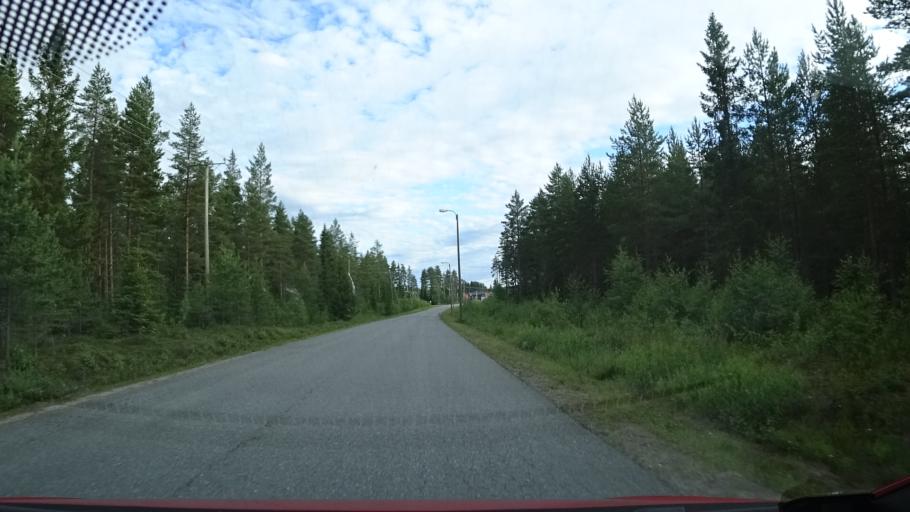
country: FI
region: Northern Ostrobothnia
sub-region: Oulu
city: Haukipudas
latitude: 65.1998
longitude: 25.4134
